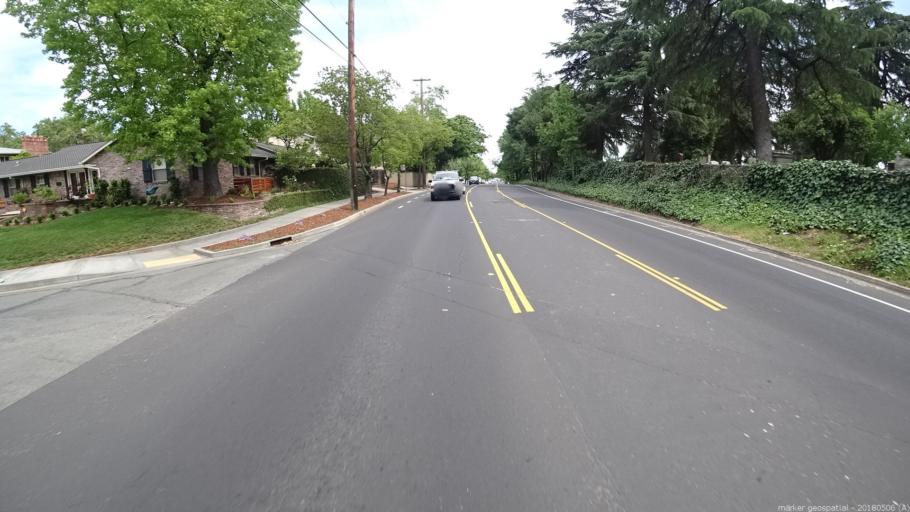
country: US
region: California
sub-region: Sacramento County
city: Sacramento
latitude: 38.5633
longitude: -121.4506
